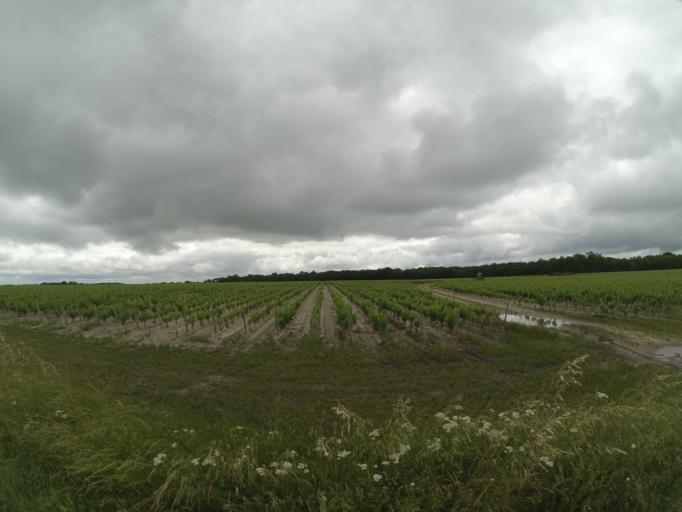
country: FR
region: Aquitaine
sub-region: Departement de la Gironde
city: Lamarque
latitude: 45.0795
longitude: -0.7274
